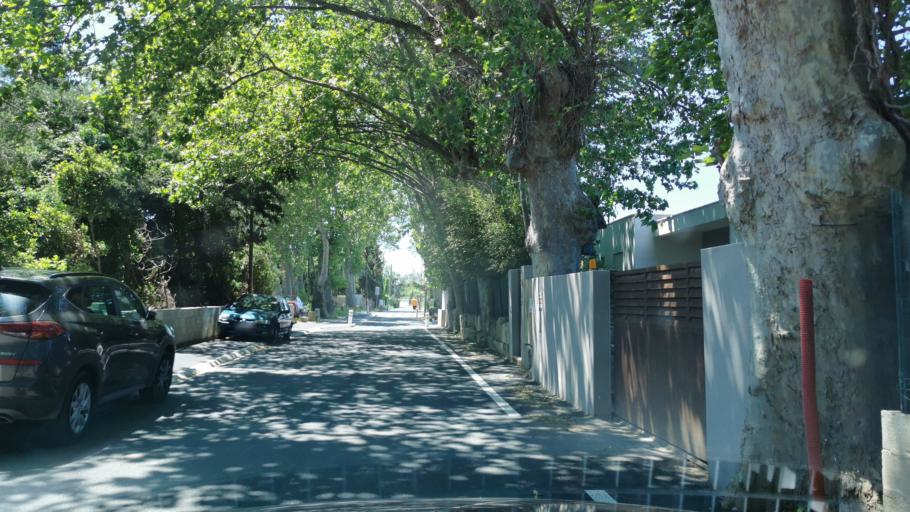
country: FR
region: Languedoc-Roussillon
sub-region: Departement de l'Aude
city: Saint-Marcel-sur-Aude
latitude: 43.2617
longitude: 2.9570
